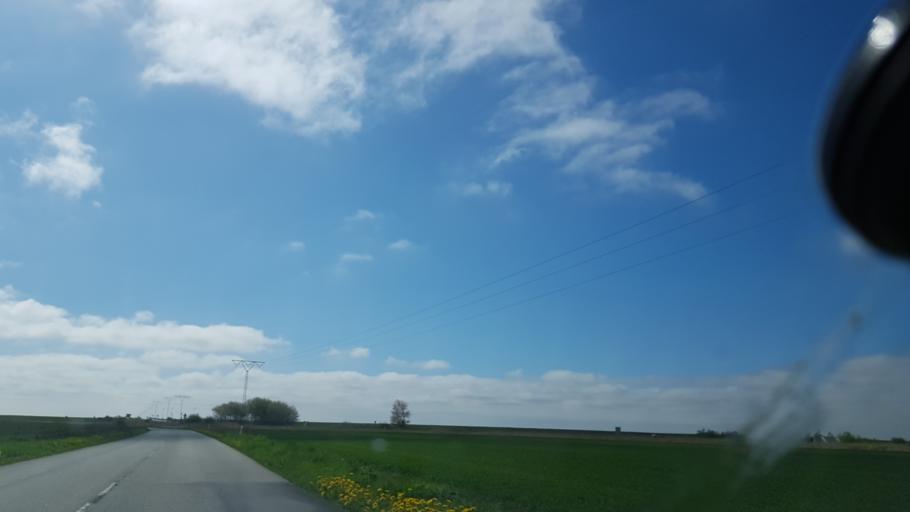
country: DK
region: South Denmark
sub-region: Tonder Kommune
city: Sherrebek
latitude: 55.1538
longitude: 8.7090
